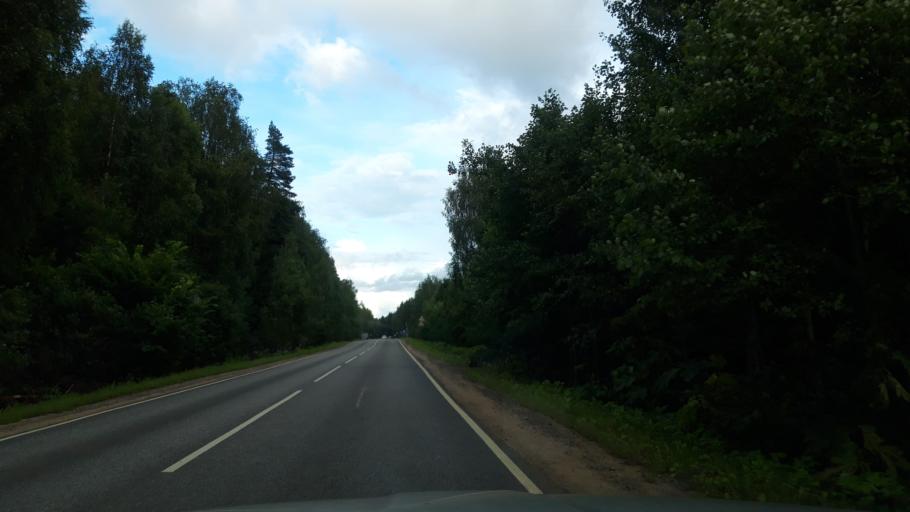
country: RU
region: Moskovskaya
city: Solnechnogorsk
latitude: 56.0964
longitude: 36.8530
